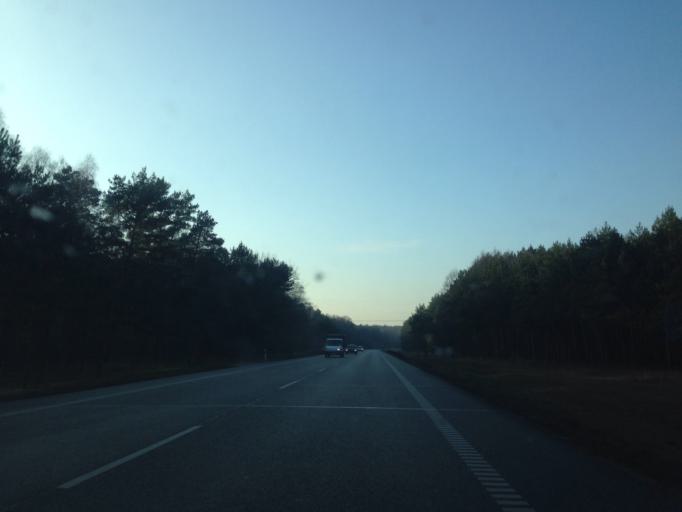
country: PL
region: Kujawsko-Pomorskie
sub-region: Powiat bydgoski
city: Solec Kujawski
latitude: 53.0612
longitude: 18.1943
